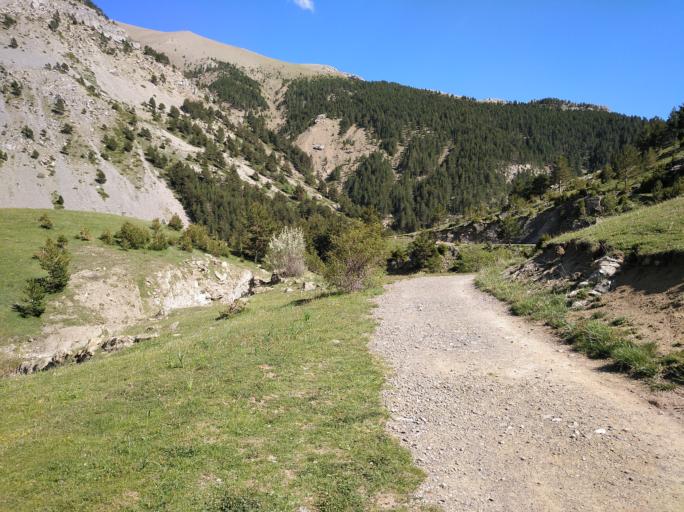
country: ES
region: Aragon
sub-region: Provincia de Huesca
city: Canfranc
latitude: 42.7414
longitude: -0.5873
